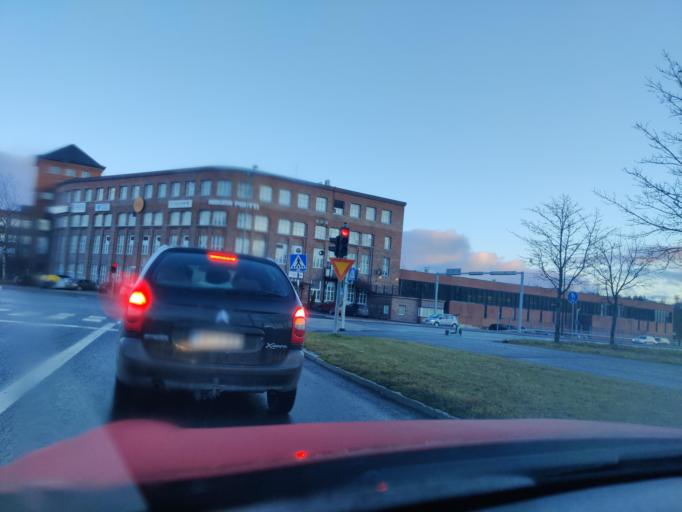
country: FI
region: Pirkanmaa
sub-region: Tampere
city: Nokia
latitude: 61.4747
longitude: 23.5047
